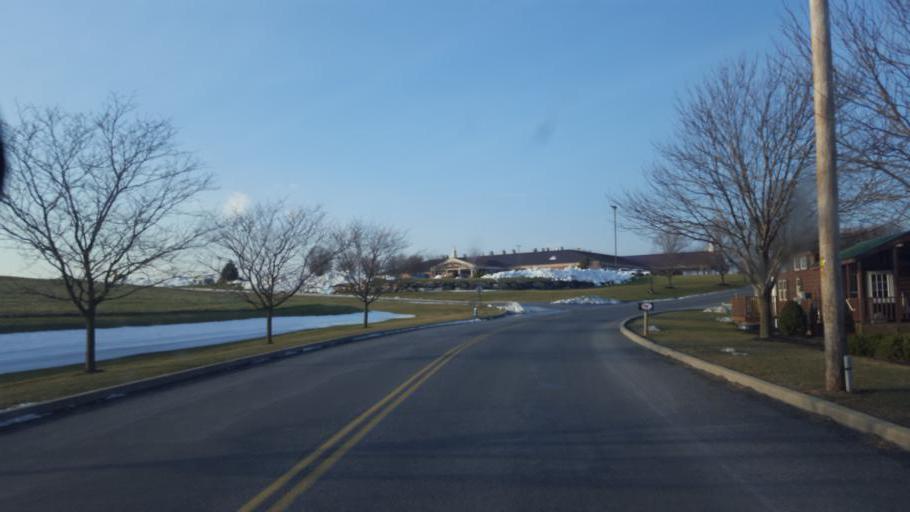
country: US
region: Pennsylvania
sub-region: Lancaster County
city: East Earl
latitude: 40.1163
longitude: -76.0322
